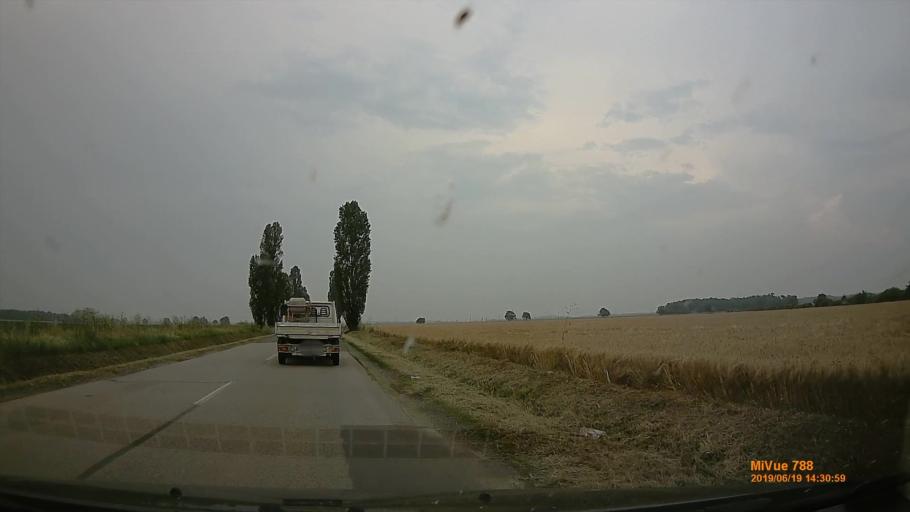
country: HU
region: Baranya
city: Szigetvar
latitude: 46.0679
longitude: 17.7690
